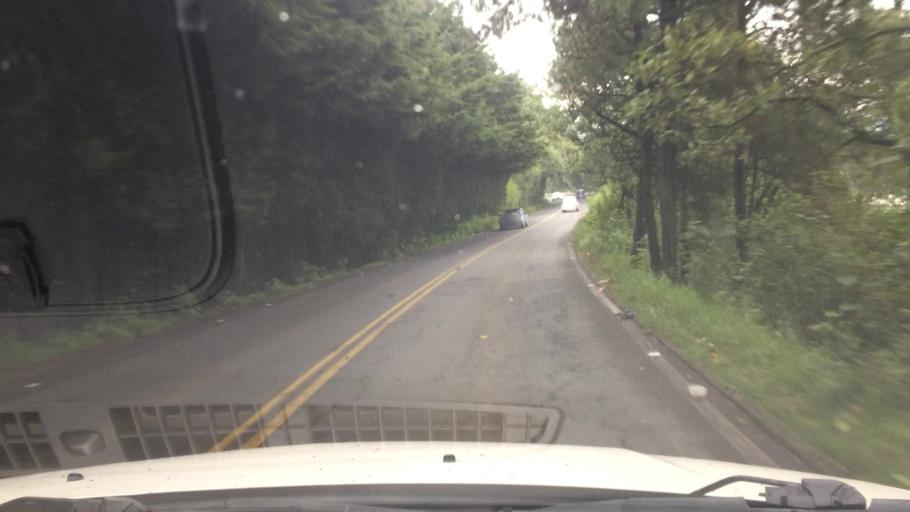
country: MX
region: Mexico City
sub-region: Tlalpan
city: Lomas de Tepemecatl
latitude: 19.2291
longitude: -99.2149
